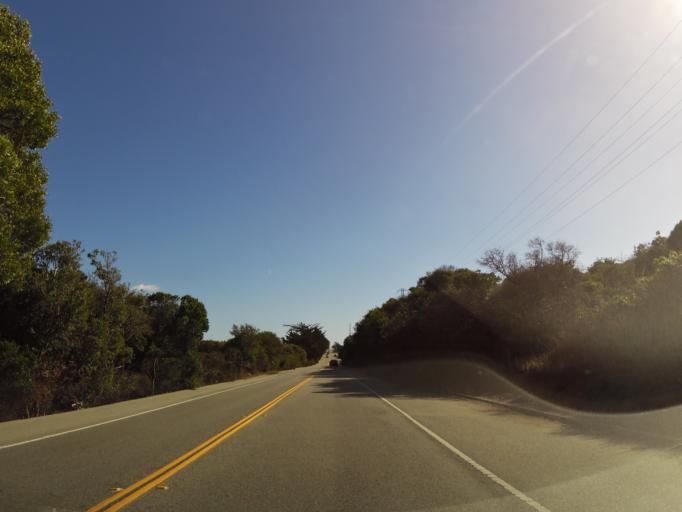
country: US
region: California
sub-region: San Mateo County
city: San Bruno
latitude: 37.6220
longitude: -122.4457
